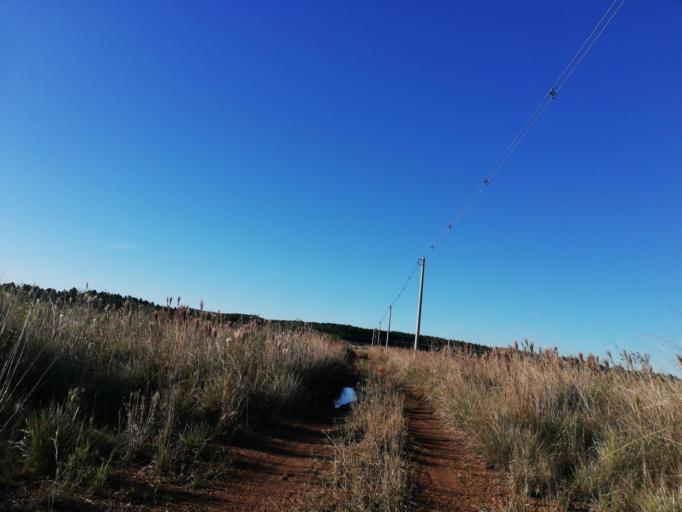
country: AR
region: Misiones
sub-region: Departamento de Candelaria
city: Candelaria
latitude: -27.4974
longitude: -55.7727
